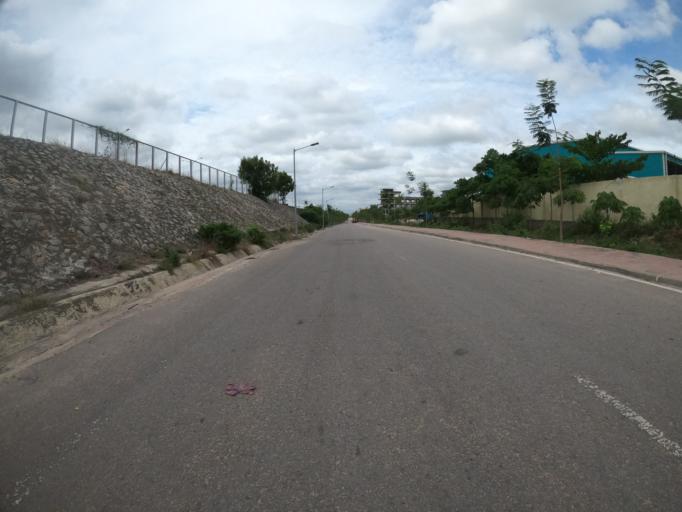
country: IN
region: Telangana
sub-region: Rangareddi
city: Sriramnagar
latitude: 17.2691
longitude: 78.3789
